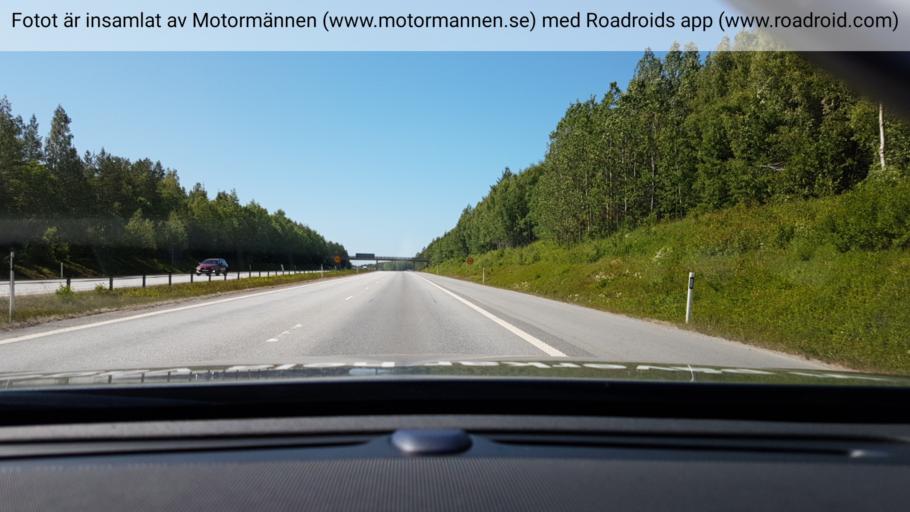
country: SE
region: Vaesterbotten
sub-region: Umea Kommun
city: Roback
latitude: 63.7945
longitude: 20.2187
